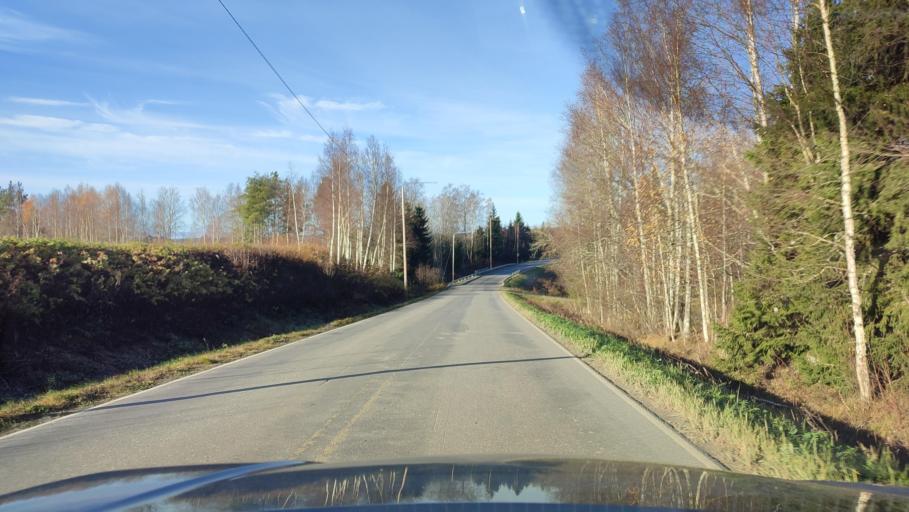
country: FI
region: Southern Ostrobothnia
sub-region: Suupohja
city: Karijoki
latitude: 62.2707
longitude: 21.7125
